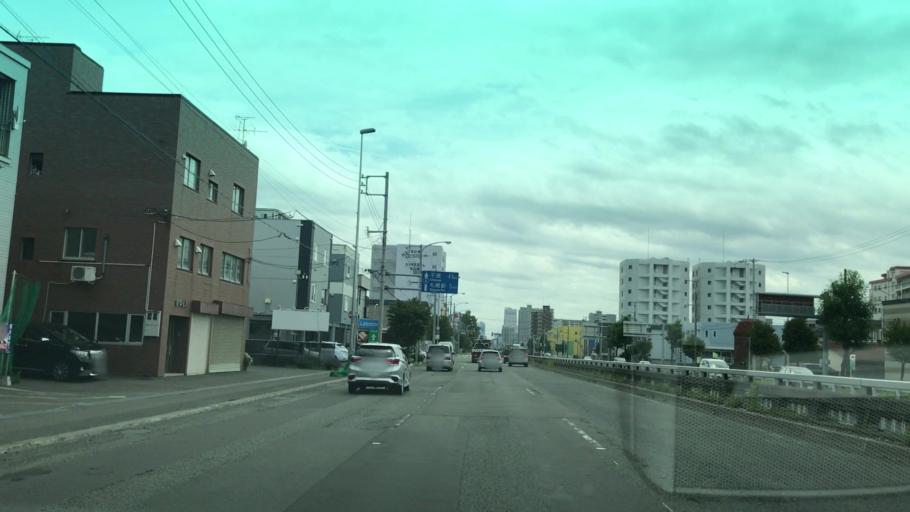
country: JP
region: Hokkaido
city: Sapporo
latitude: 43.1000
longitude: 141.3454
